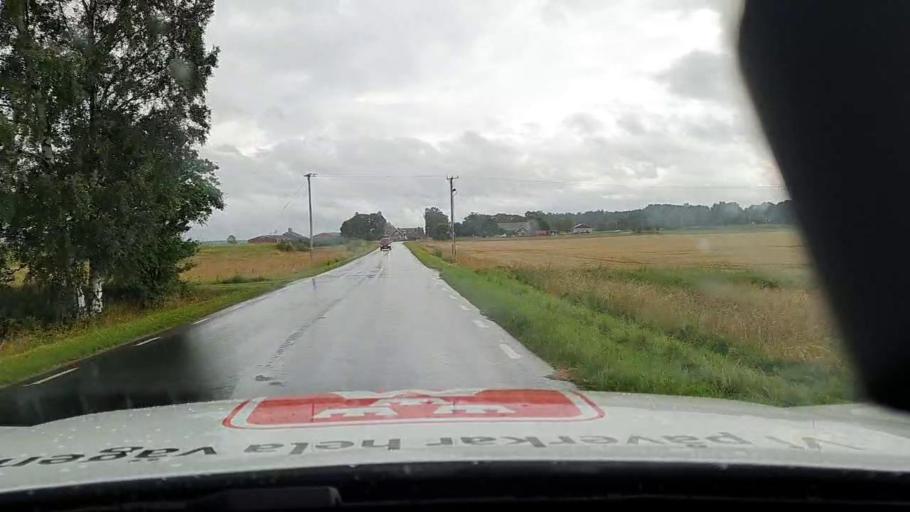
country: SE
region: Vaestra Goetaland
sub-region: Skovde Kommun
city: Stopen
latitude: 58.5575
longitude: 13.9809
